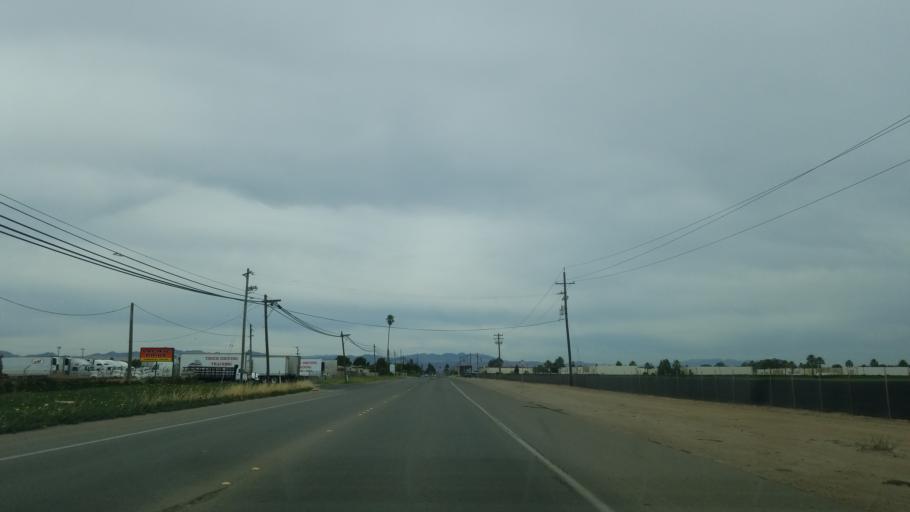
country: US
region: California
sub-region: Santa Barbara County
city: Santa Maria
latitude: 34.9208
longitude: -120.4699
